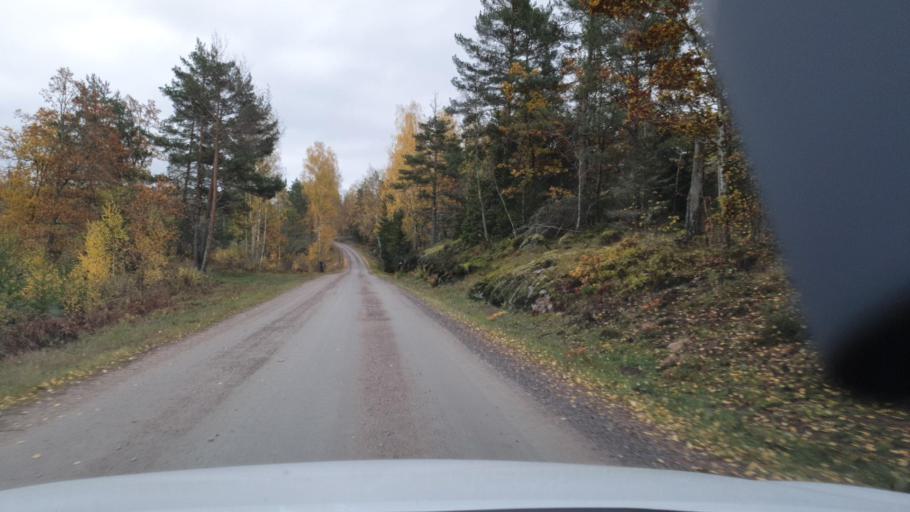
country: SE
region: Kalmar
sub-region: Vasterviks Kommun
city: Ankarsrum
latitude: 57.6937
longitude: 16.4667
